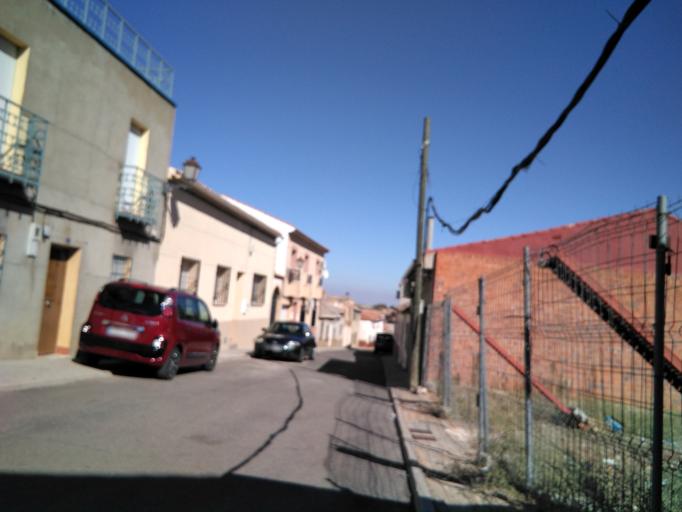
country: ES
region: Castille-La Mancha
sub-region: Provincia de Ciudad Real
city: Ballesteros de Calatrava
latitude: 38.8328
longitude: -3.9461
